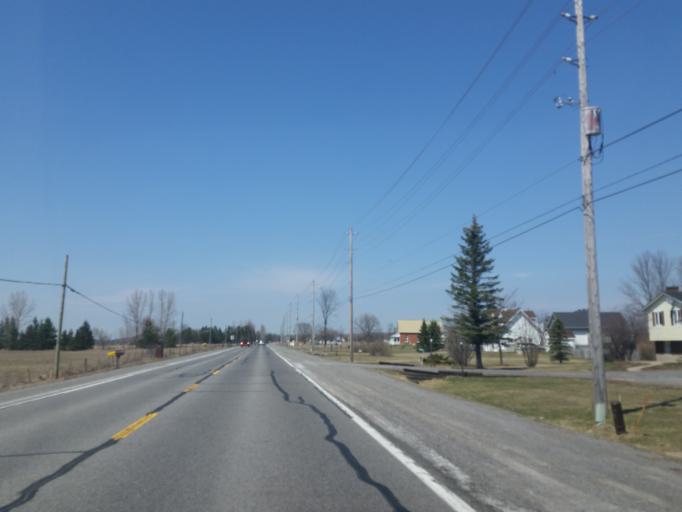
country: CA
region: Ontario
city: Bells Corners
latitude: 45.4481
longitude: -76.0564
